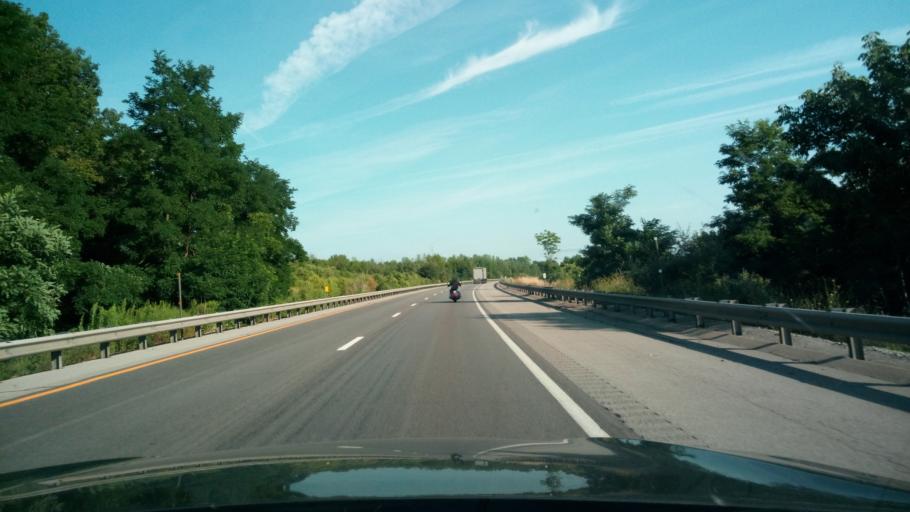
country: US
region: New York
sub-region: Livingston County
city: Dansville
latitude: 42.5837
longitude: -77.7447
